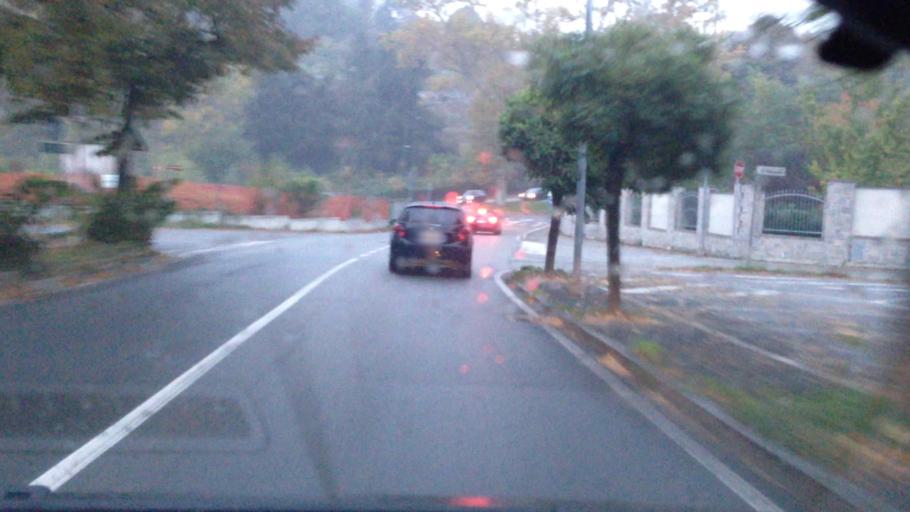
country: IT
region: Piedmont
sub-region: Provincia di Asti
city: Asti
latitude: 44.9141
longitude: 8.2115
